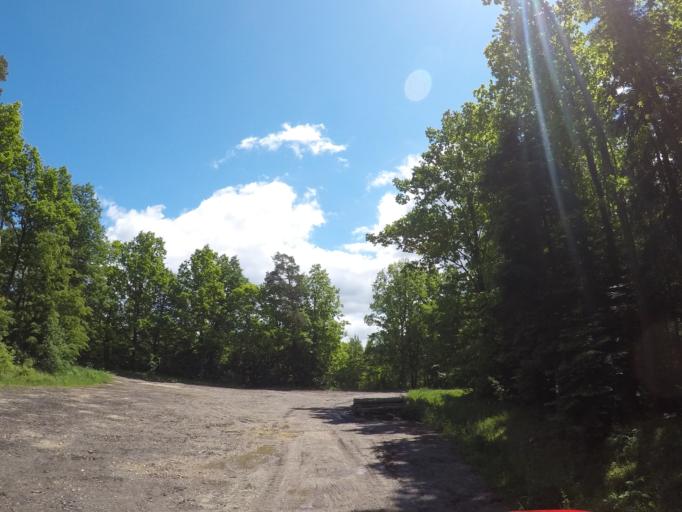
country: PL
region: Swietokrzyskie
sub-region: Powiat kielecki
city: Domaszowice
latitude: 50.9100
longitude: 20.6613
